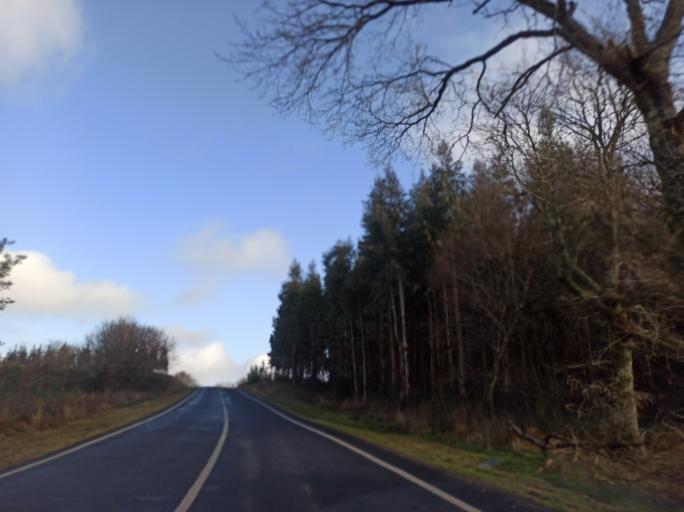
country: ES
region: Galicia
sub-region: Provincia da Coruna
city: Sobrado
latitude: 43.0813
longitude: -8.0039
